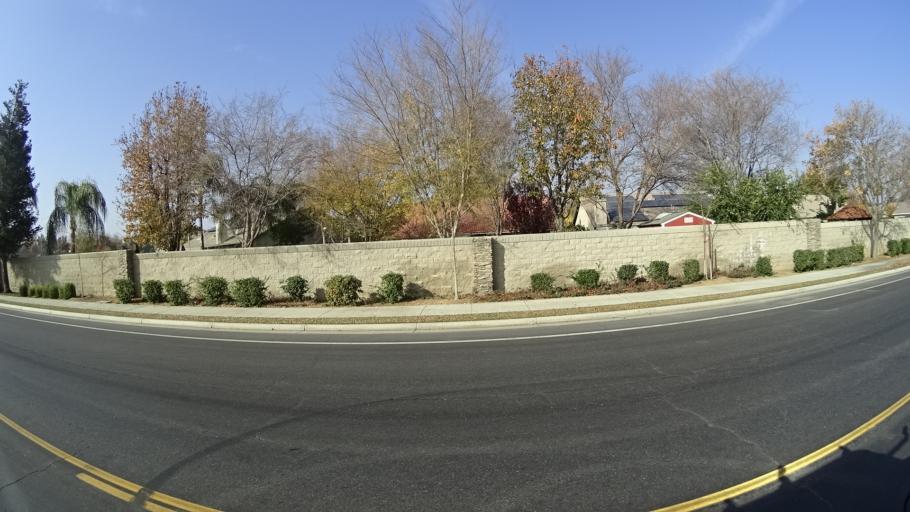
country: US
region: California
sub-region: Kern County
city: Greenacres
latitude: 35.4129
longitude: -119.1183
